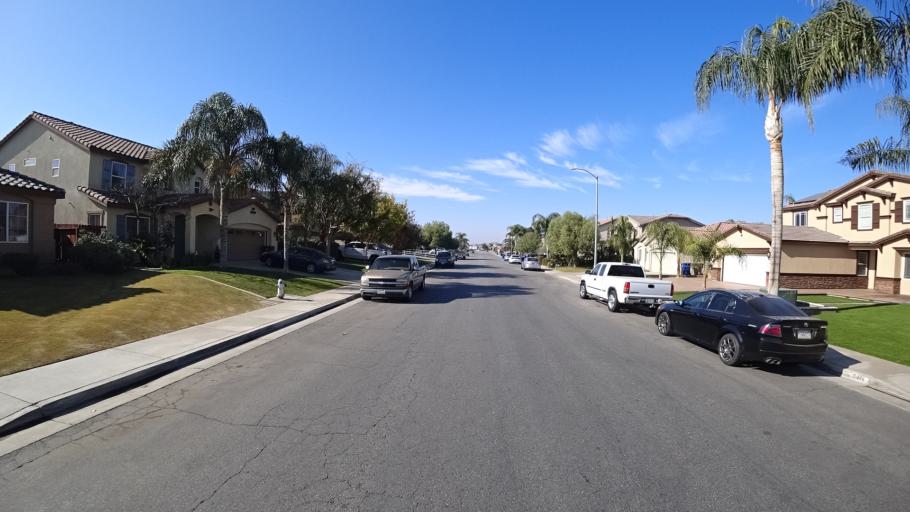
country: US
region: California
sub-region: Kern County
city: Greenfield
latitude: 35.2801
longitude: -119.0628
